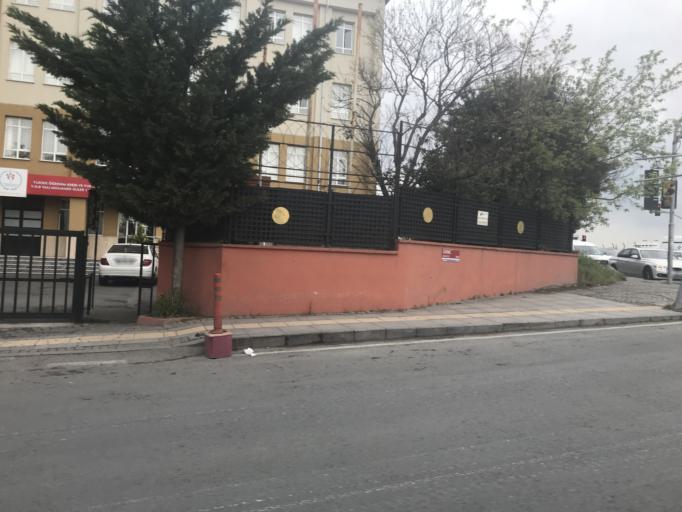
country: TR
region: Istanbul
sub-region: Atasehir
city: Atasehir
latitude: 40.9855
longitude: 29.1371
